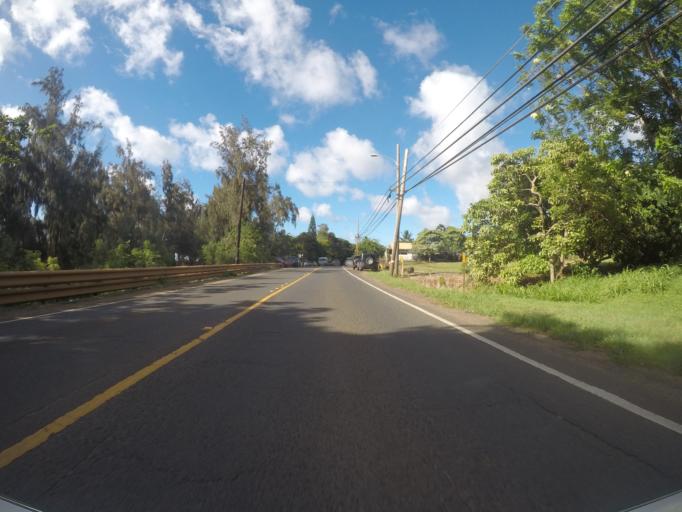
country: US
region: Hawaii
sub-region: Honolulu County
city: Pupukea
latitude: 21.6576
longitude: -158.0579
